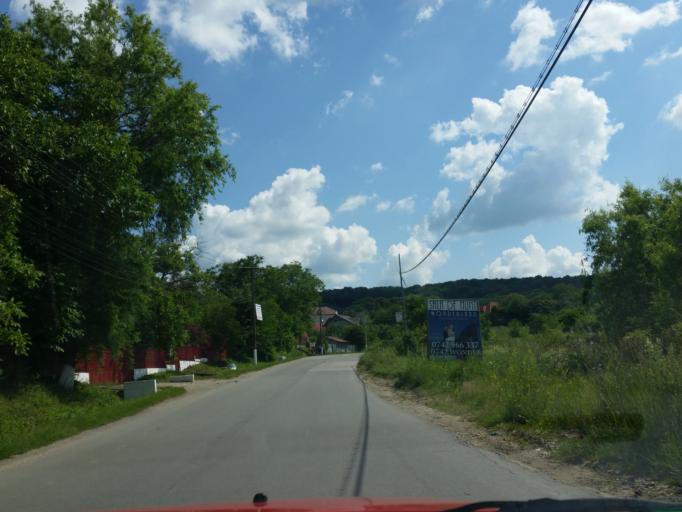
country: RO
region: Cluj
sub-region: Comuna Feleacu
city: Feleacu
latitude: 46.7312
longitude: 23.5872
